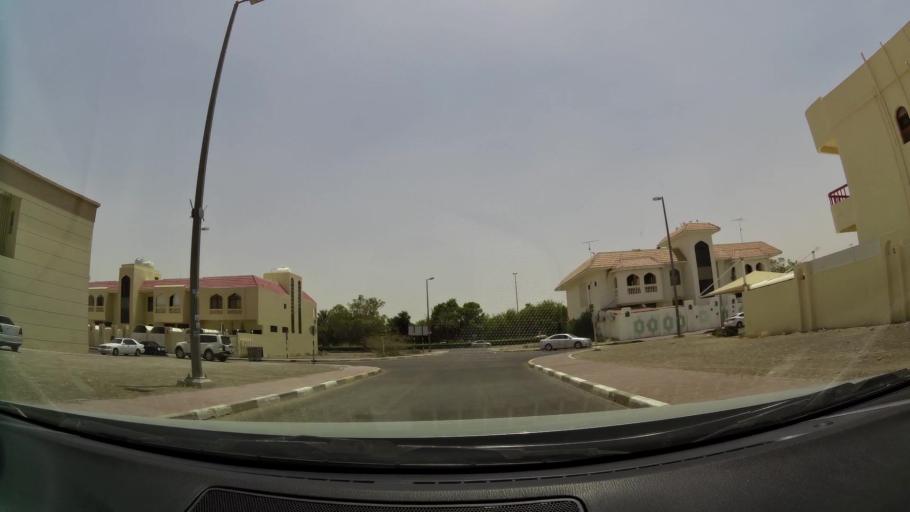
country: AE
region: Abu Dhabi
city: Al Ain
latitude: 24.2063
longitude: 55.7135
